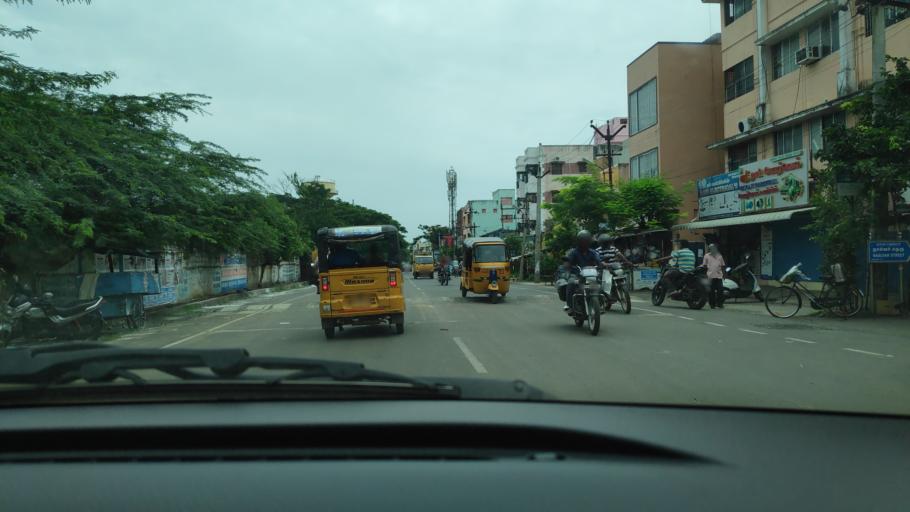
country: IN
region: Tamil Nadu
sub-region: Kancheepuram
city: Pallavaram
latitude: 12.9274
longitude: 80.1267
